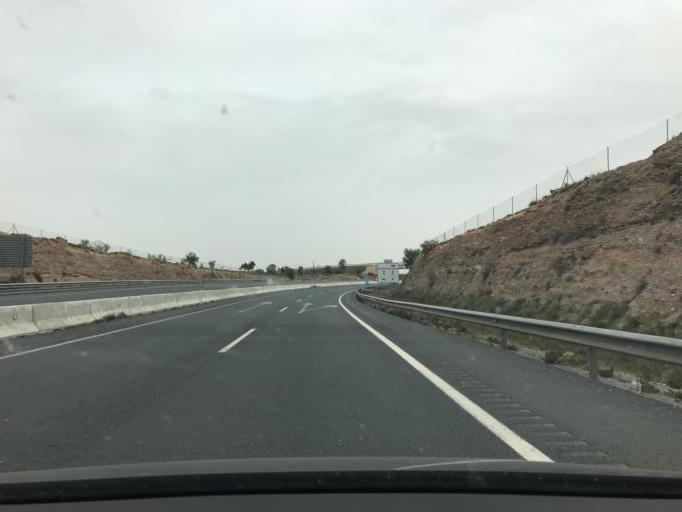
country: ES
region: Andalusia
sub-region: Provincia de Granada
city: Gor
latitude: 37.3954
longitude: -2.9937
